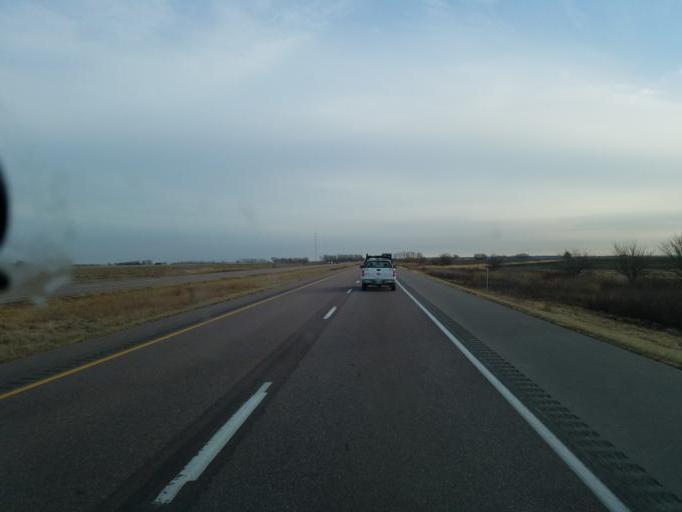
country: US
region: Iowa
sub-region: Monona County
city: Onawa
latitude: 42.0963
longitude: -96.1852
